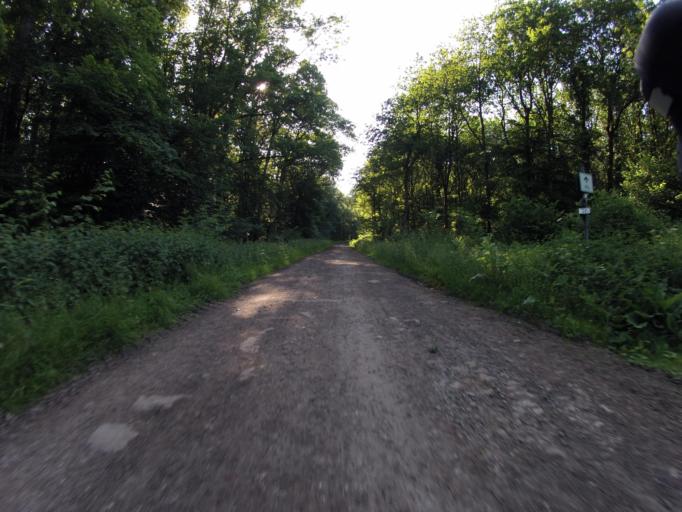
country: DE
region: Lower Saxony
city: Suddendorf
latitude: 52.3092
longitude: 7.2692
